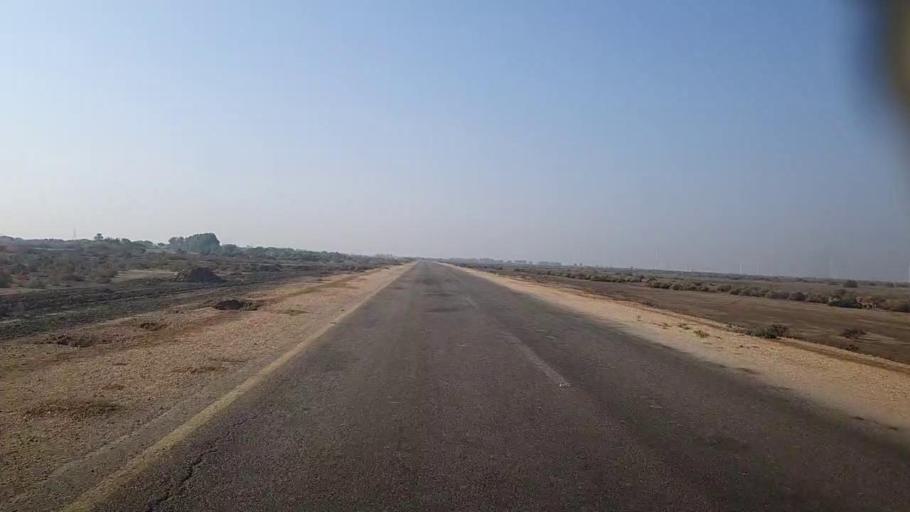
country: PK
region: Sindh
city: Gharo
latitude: 24.6977
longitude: 67.5261
